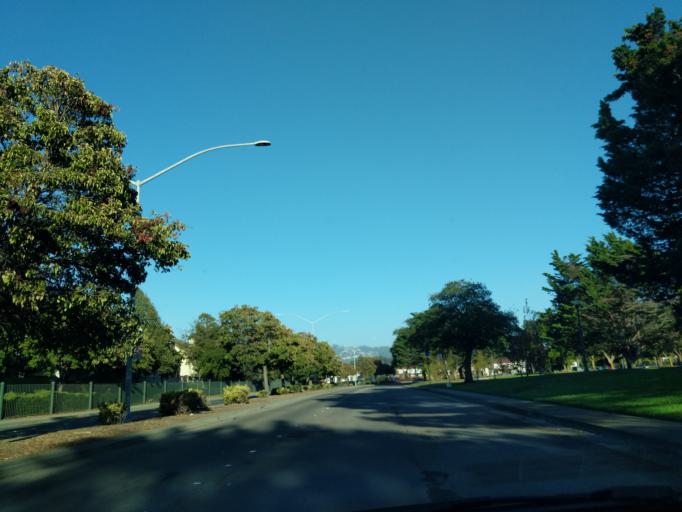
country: US
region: California
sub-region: Contra Costa County
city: Richmond
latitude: 37.9160
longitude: -122.3470
